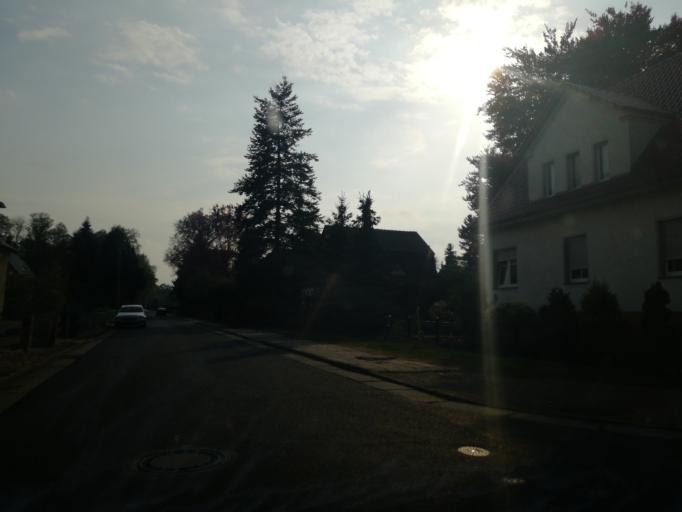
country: DE
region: Brandenburg
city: Calau
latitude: 51.7432
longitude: 13.9679
